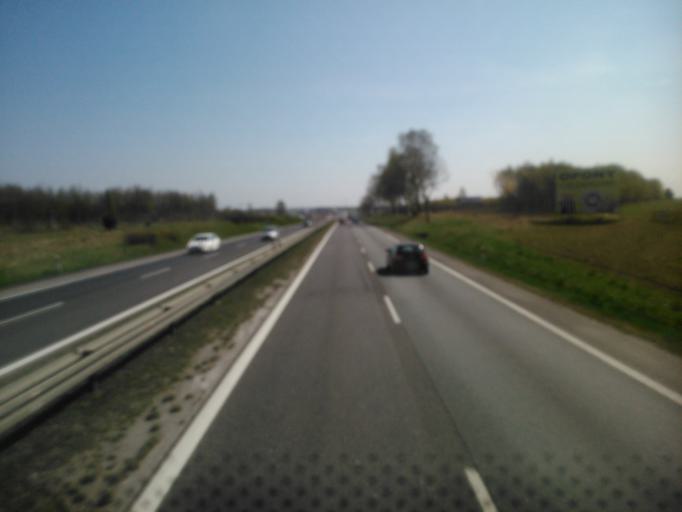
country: PL
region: Silesian Voivodeship
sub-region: Powiat myszkowski
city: Kozieglowy
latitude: 50.6267
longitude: 19.1419
